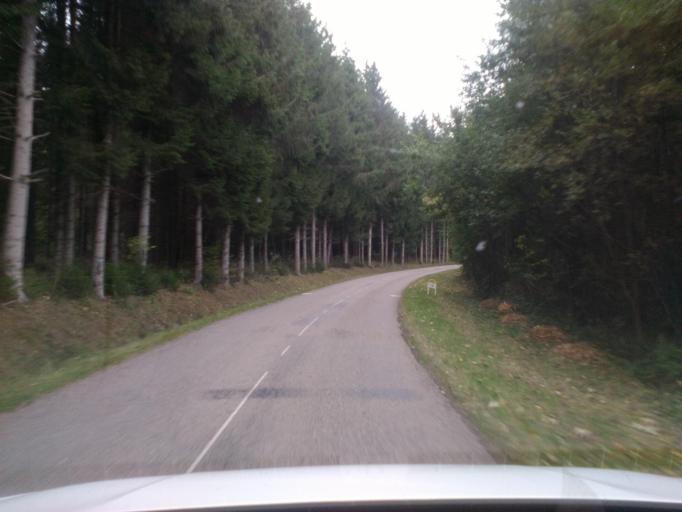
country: FR
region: Lorraine
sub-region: Departement des Vosges
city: Sainte-Marguerite
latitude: 48.3255
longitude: 7.0231
